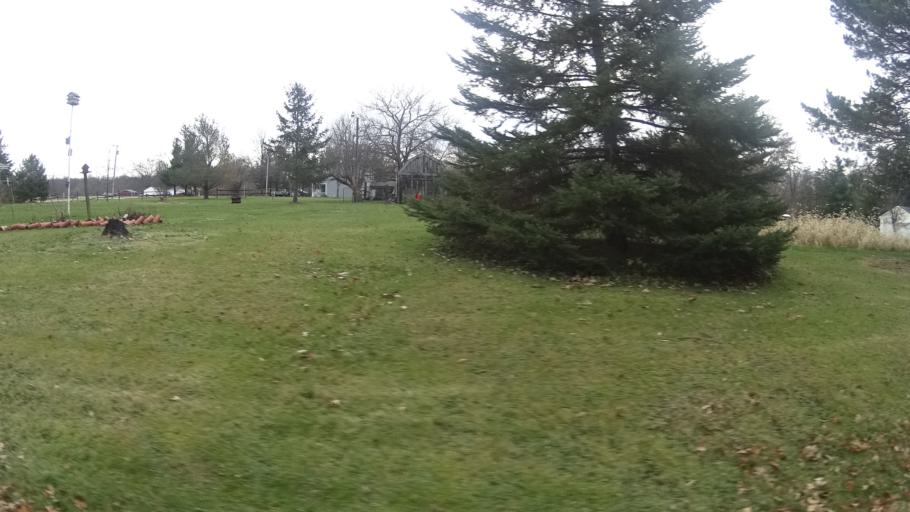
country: US
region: Ohio
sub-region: Cuyahoga County
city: Strongsville
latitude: 41.2894
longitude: -81.8789
